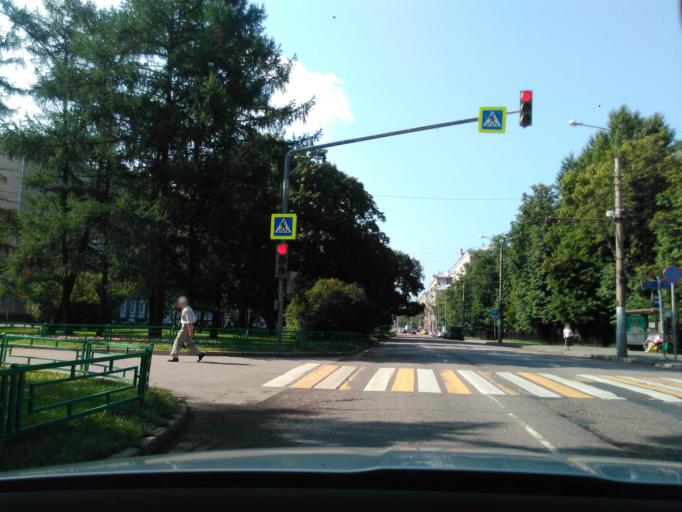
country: RU
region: Moscow
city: Sokol
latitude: 55.7987
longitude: 37.5144
